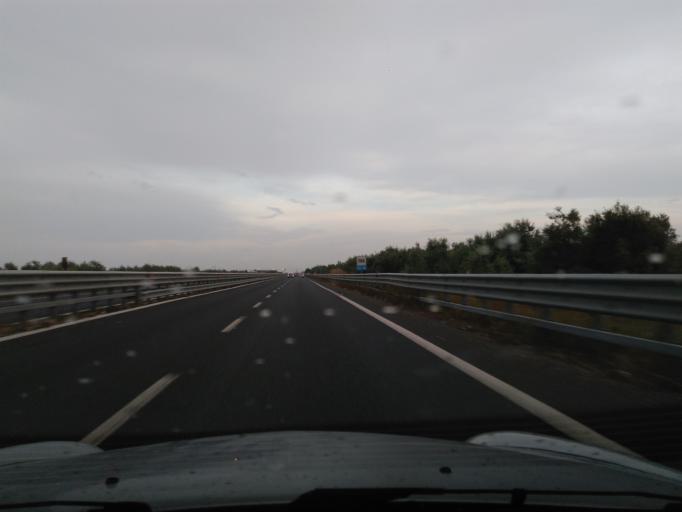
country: IT
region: Apulia
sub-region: Provincia di Bari
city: Giovinazzo
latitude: 41.1645
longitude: 16.7114
